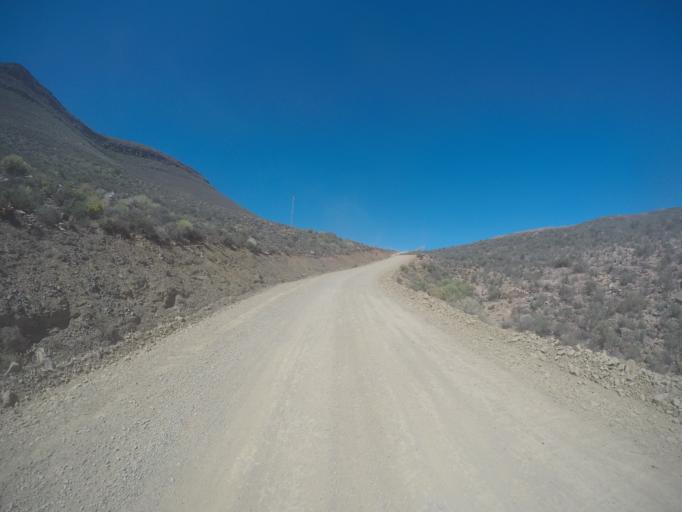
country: ZA
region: Western Cape
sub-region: West Coast District Municipality
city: Clanwilliam
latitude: -32.6043
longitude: 19.3686
